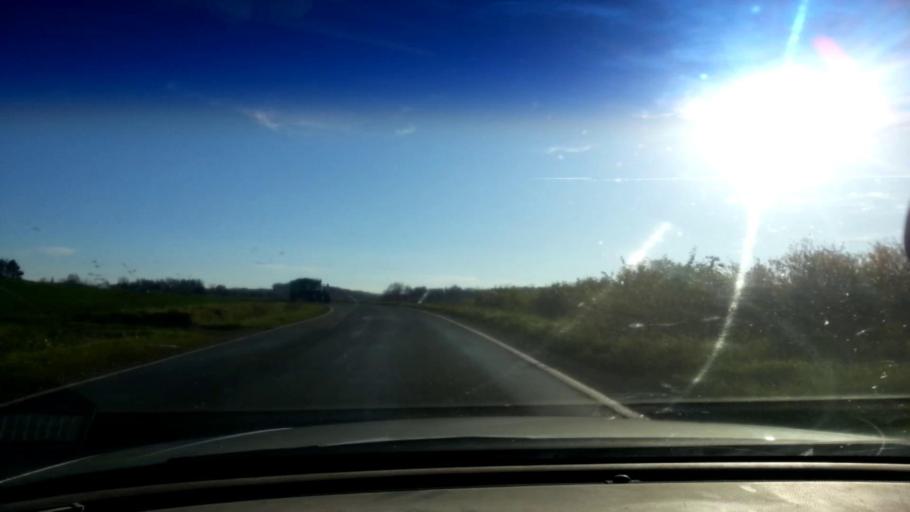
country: DE
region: Bavaria
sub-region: Upper Franconia
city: Poxdorf
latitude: 49.9168
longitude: 11.0894
